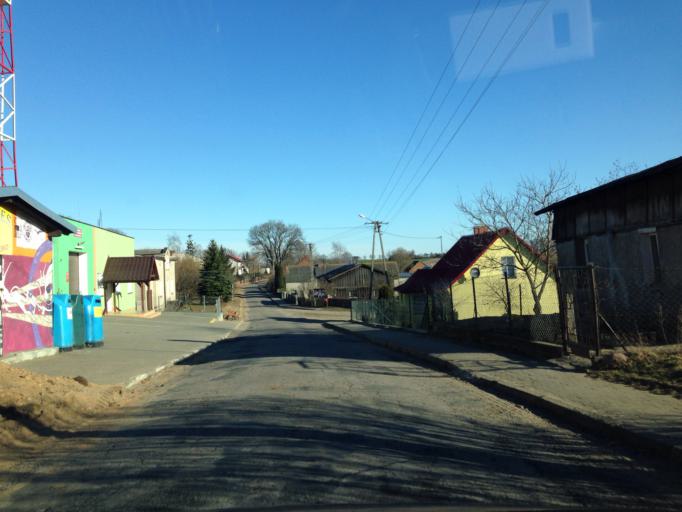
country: PL
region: Kujawsko-Pomorskie
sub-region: Powiat brodnicki
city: Brzozie
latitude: 53.3728
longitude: 19.6278
